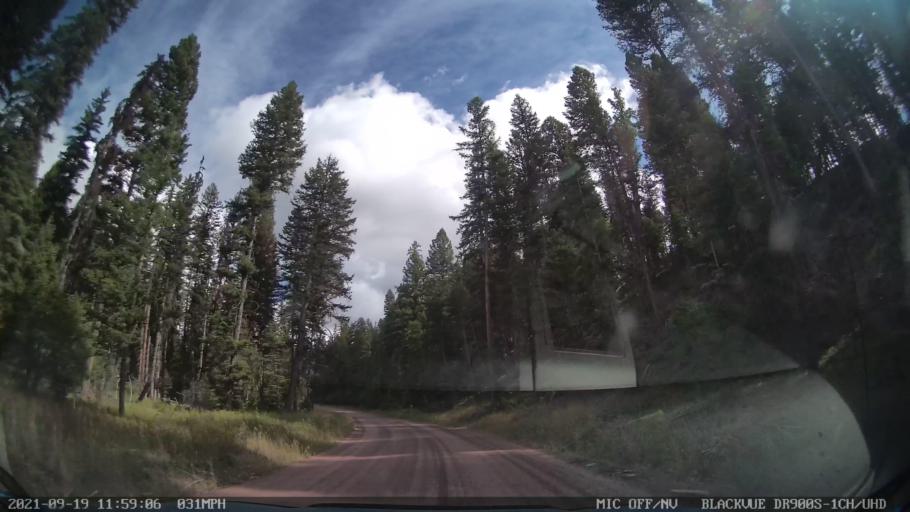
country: US
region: Montana
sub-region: Missoula County
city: Seeley Lake
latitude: 47.1833
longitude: -113.4794
